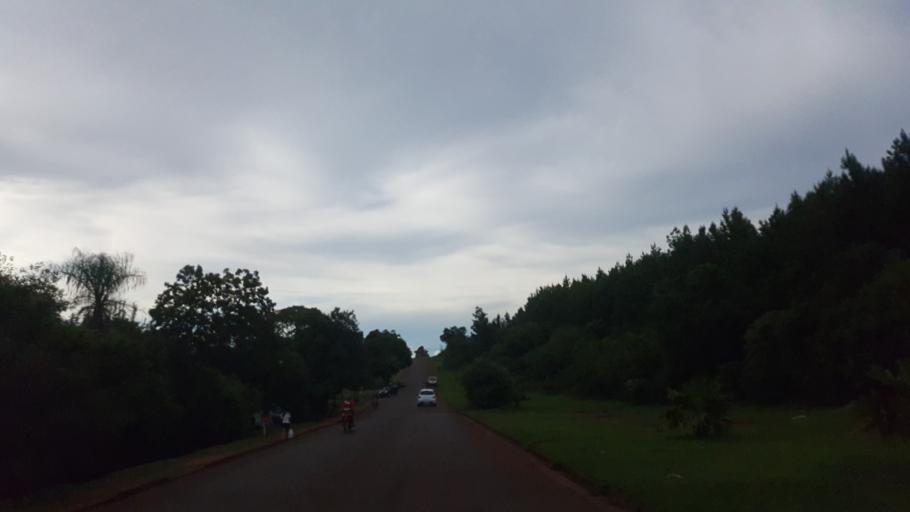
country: AR
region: Misiones
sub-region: Departamento de San Ignacio
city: San Ignacio
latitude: -27.2634
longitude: -55.5289
